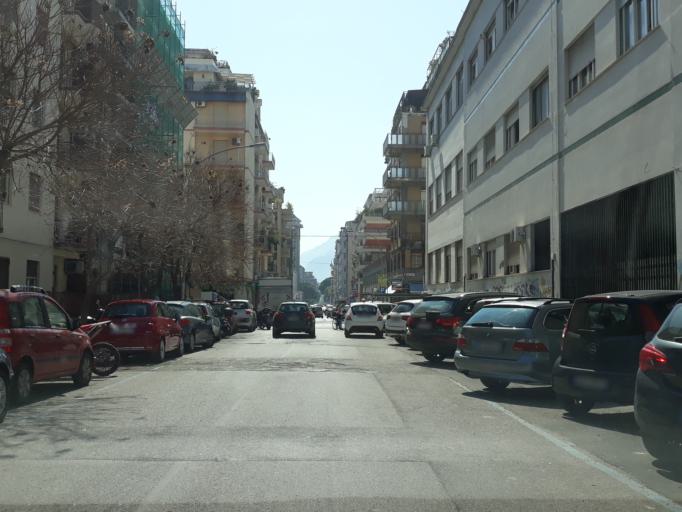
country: IT
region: Sicily
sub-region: Palermo
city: Palermo
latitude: 38.1375
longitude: 13.3516
